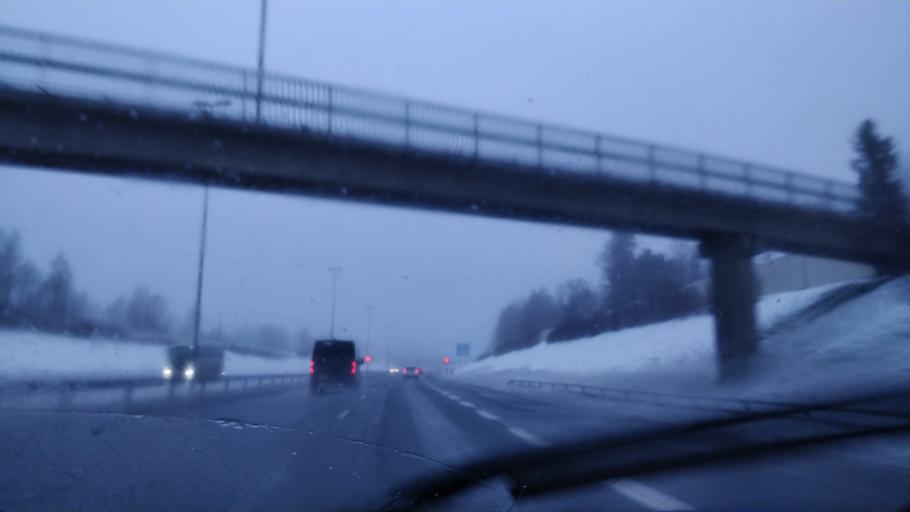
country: FI
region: Lapland
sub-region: Kemi-Tornio
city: Kemi
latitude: 65.7468
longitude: 24.5794
